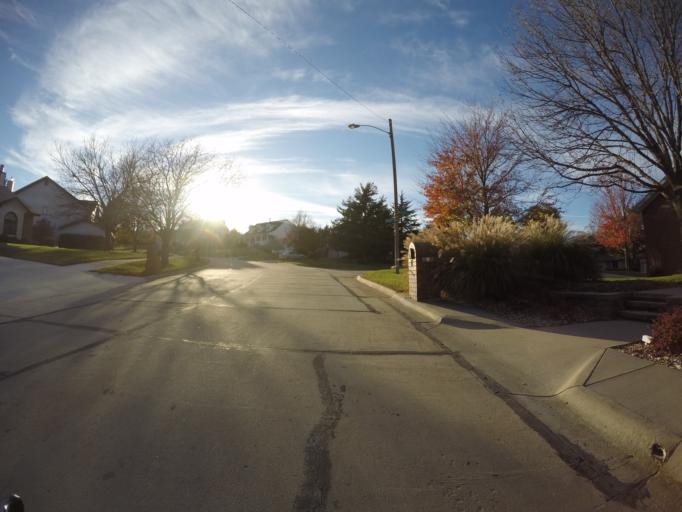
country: US
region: Kansas
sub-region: Riley County
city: Manhattan
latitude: 39.2009
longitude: -96.6342
